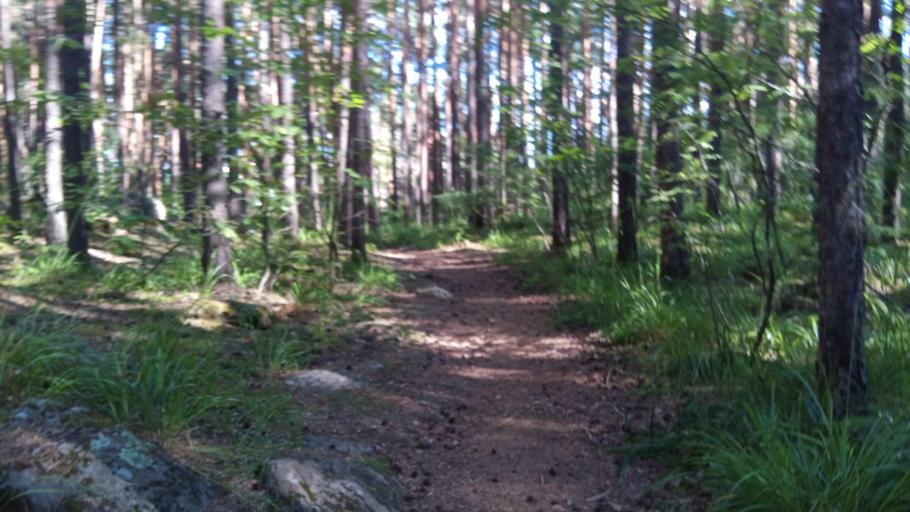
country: RU
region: Chelyabinsk
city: Chebarkul'
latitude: 55.0192
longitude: 60.3150
